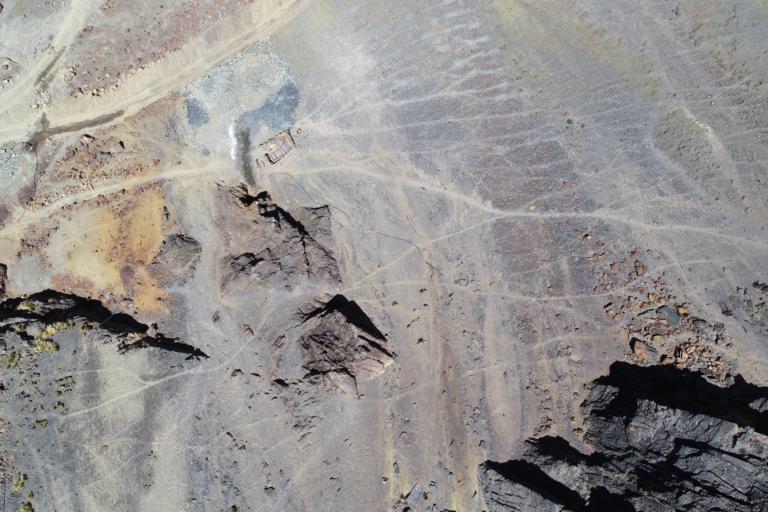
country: BO
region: La Paz
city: La Paz
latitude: -16.6198
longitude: -67.8252
